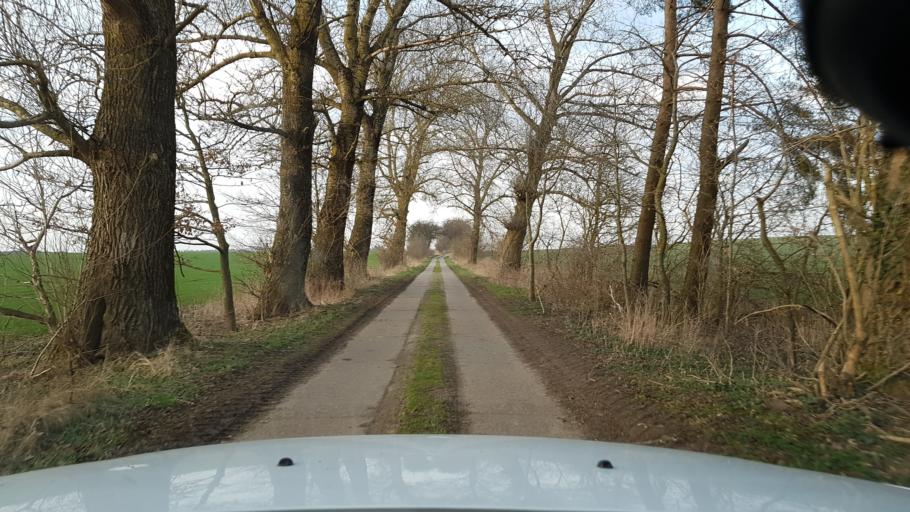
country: PL
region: West Pomeranian Voivodeship
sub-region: Koszalin
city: Koszalin
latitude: 54.0903
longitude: 16.1333
